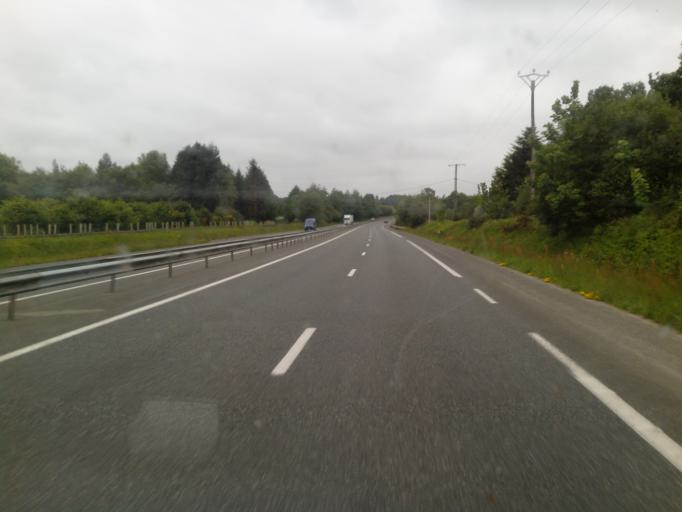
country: FR
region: Brittany
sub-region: Departement du Finistere
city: Guerlesquin
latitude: 48.5677
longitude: -3.5614
